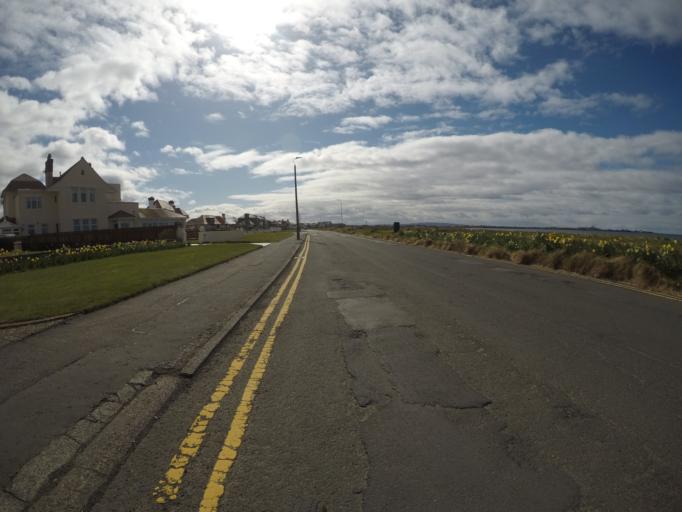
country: GB
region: Scotland
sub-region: South Ayrshire
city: Troon
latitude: 55.5635
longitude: -4.6577
